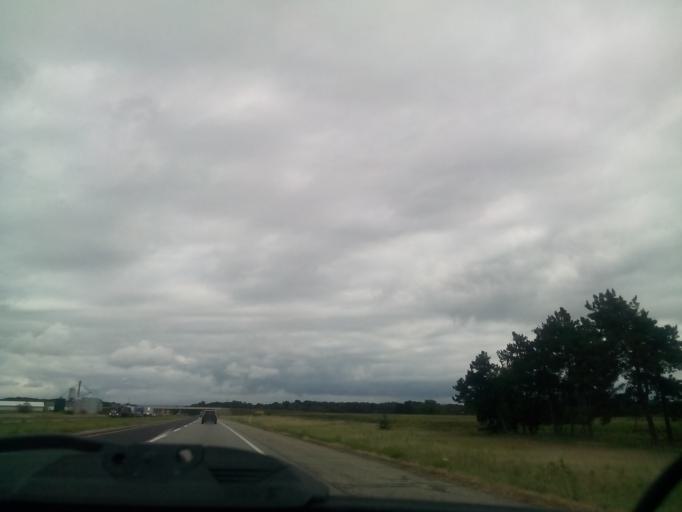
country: US
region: Michigan
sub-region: Saint Joseph County
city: Sturgis
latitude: 41.7442
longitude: -85.3226
